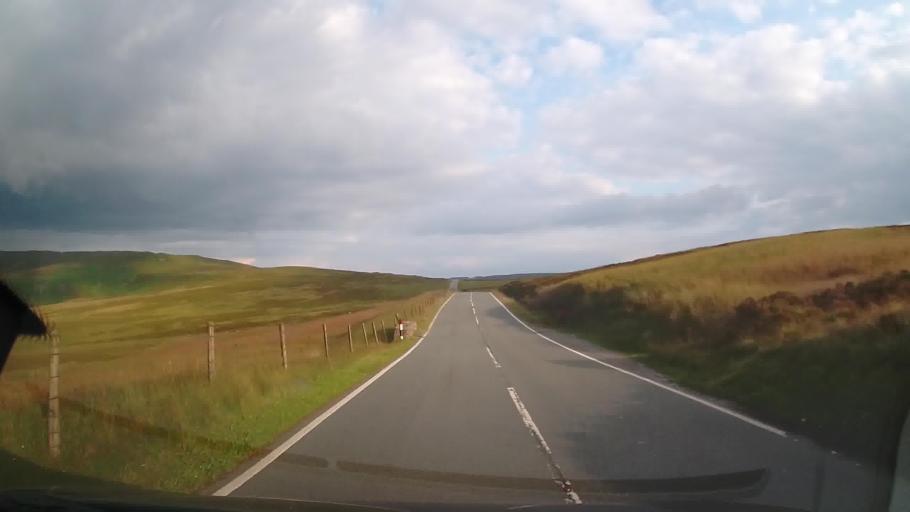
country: GB
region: Wales
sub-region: Denbighshire
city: Llandrillo
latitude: 52.8696
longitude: -3.4679
